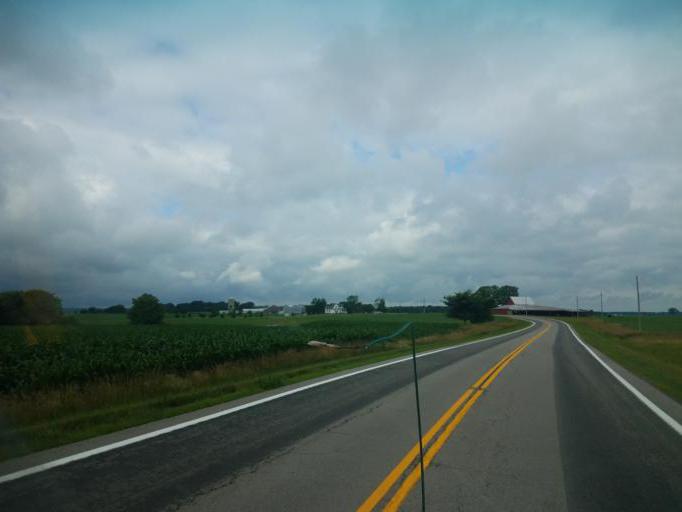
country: US
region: Ohio
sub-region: Champaign County
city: North Lewisburg
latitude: 40.4072
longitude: -83.5597
